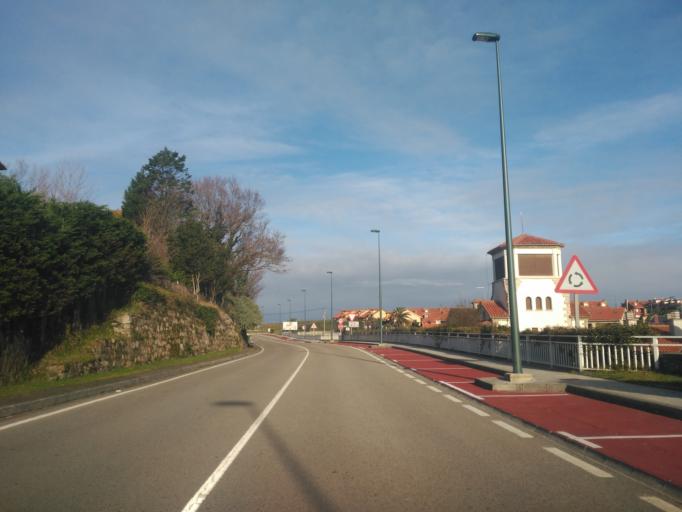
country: ES
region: Cantabria
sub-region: Provincia de Cantabria
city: Comillas
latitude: 43.3896
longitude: -4.2906
